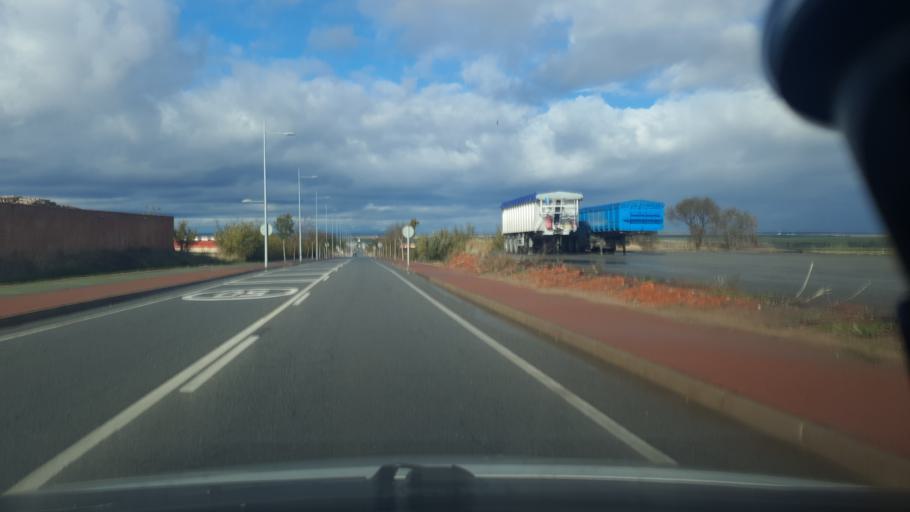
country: ES
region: Castille and Leon
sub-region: Provincia de Segovia
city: Carbonero el Mayor
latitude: 41.1285
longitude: -4.2688
